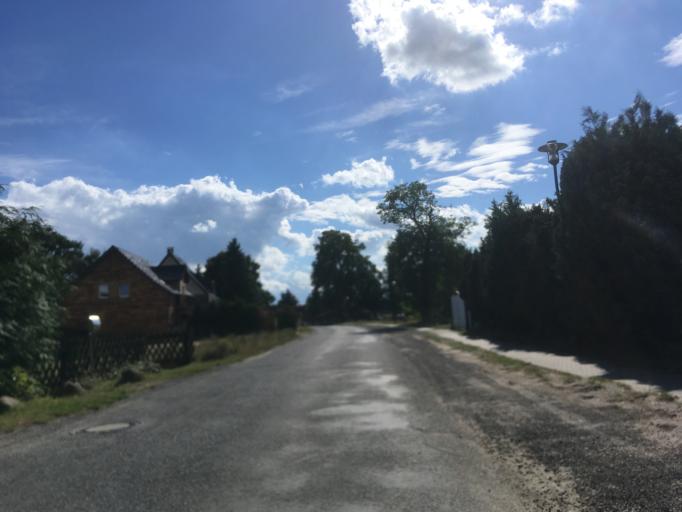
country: DE
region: Brandenburg
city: Angermunde
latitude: 52.9739
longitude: 13.9865
